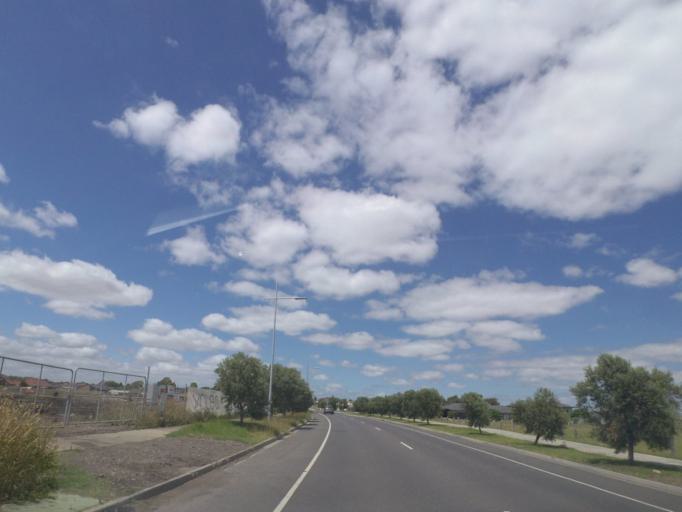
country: AU
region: Victoria
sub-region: Whittlesea
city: Lalor
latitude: -37.6664
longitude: 144.9956
